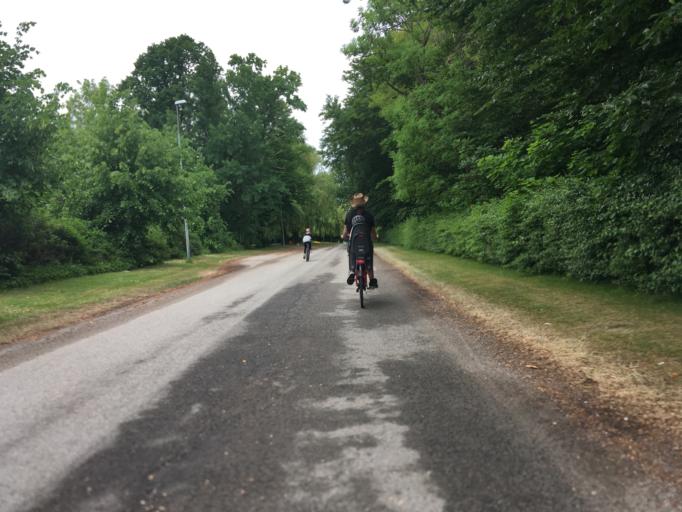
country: SE
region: Skane
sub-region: Staffanstorps Kommun
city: Hjaerup
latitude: 55.6997
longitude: 13.1420
